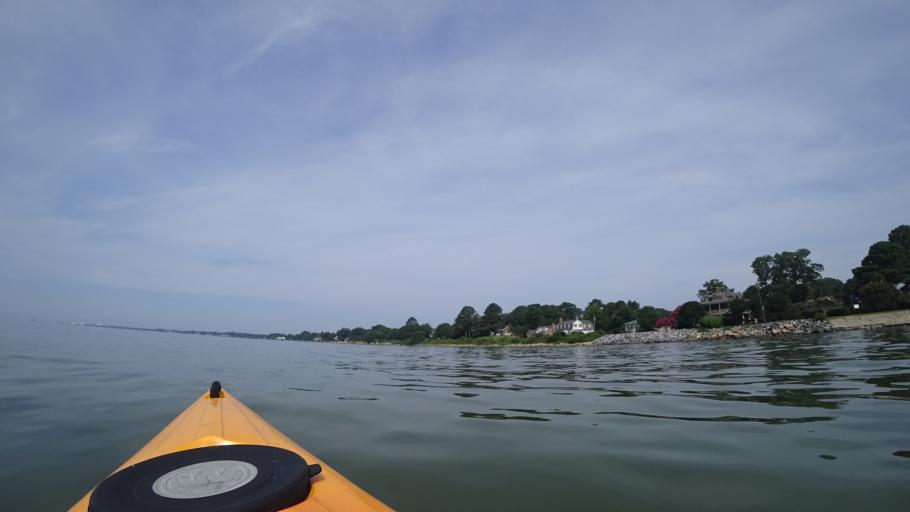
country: US
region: Virginia
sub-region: City of Hampton
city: Hampton
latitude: 37.0022
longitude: -76.3585
